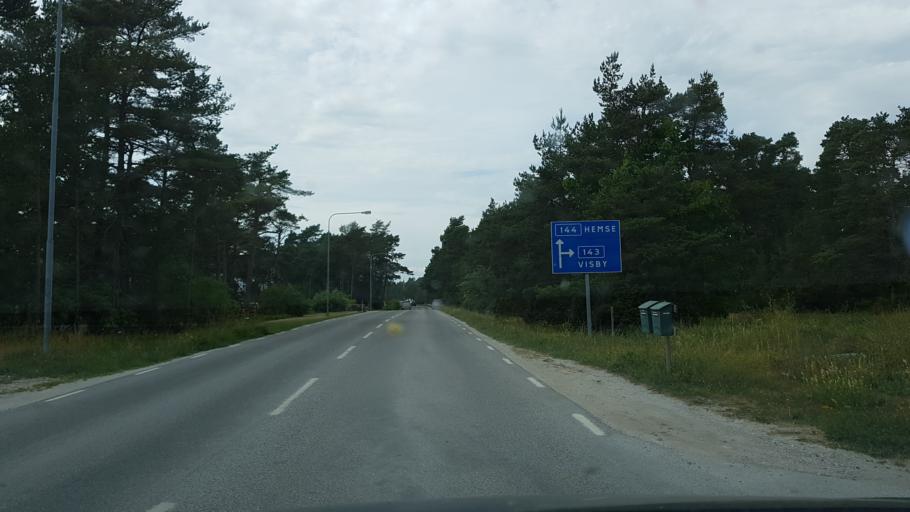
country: SE
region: Gotland
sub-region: Gotland
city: Hemse
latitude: 57.3392
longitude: 18.6969
